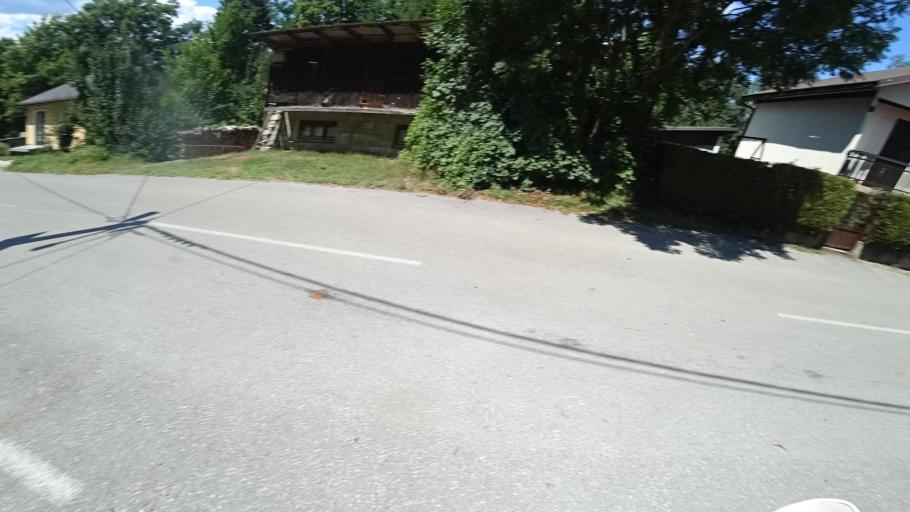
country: HR
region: Karlovacka
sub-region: Grad Ogulin
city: Ogulin
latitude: 45.2535
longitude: 15.2170
